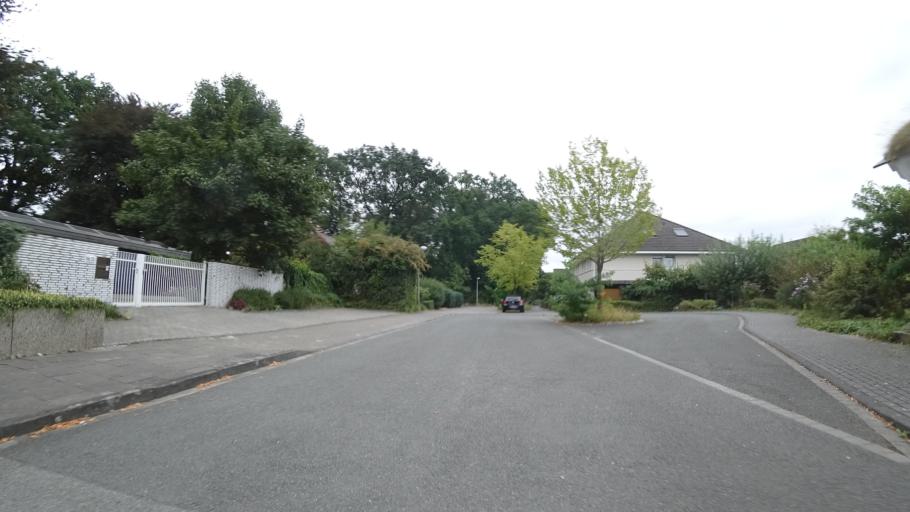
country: DE
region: North Rhine-Westphalia
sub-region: Regierungsbezirk Detmold
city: Guetersloh
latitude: 51.9151
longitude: 8.4342
